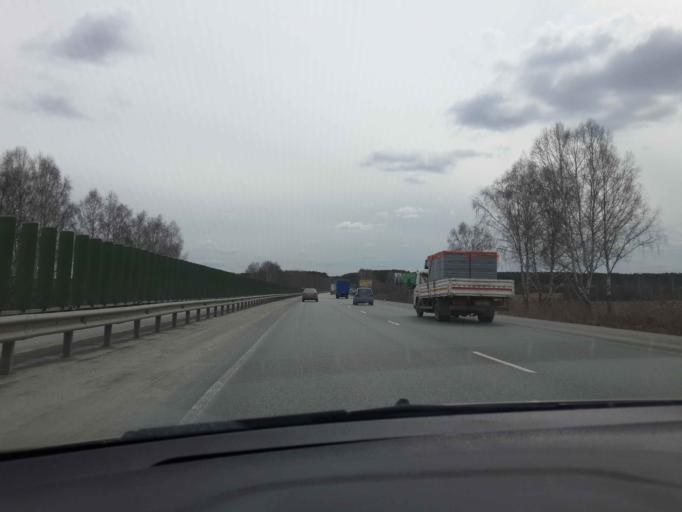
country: RU
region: Sverdlovsk
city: Istok
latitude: 56.7919
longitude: 60.8271
